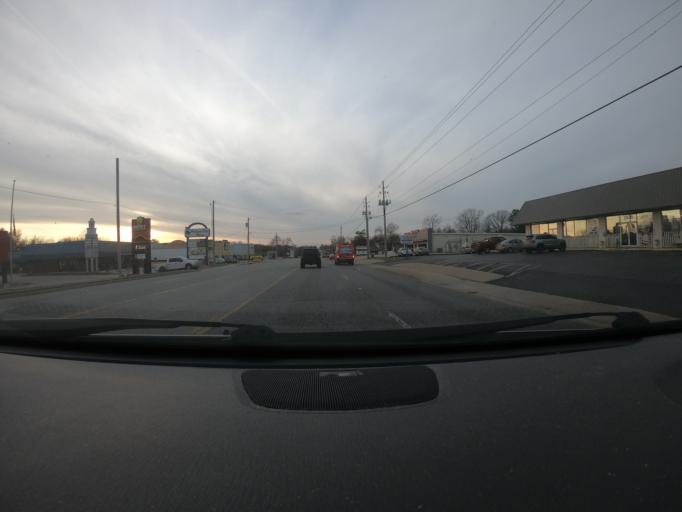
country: US
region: Arkansas
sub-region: Benton County
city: Rogers
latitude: 36.3344
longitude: -94.1577
